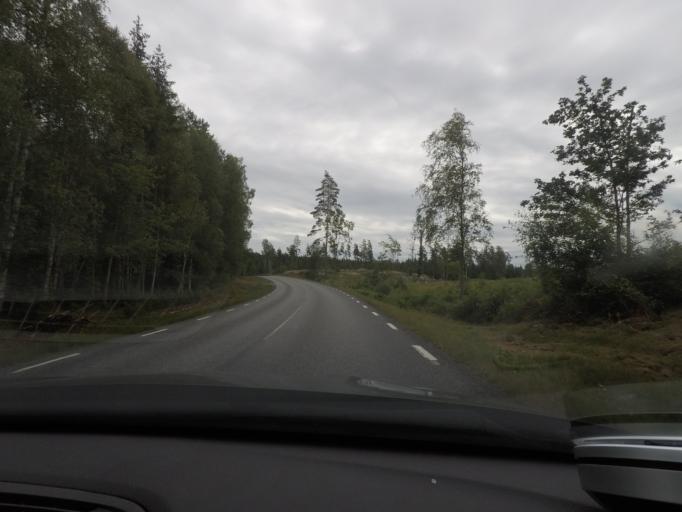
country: SE
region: Skane
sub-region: Osby Kommun
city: Lonsboda
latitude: 56.4369
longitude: 14.4681
